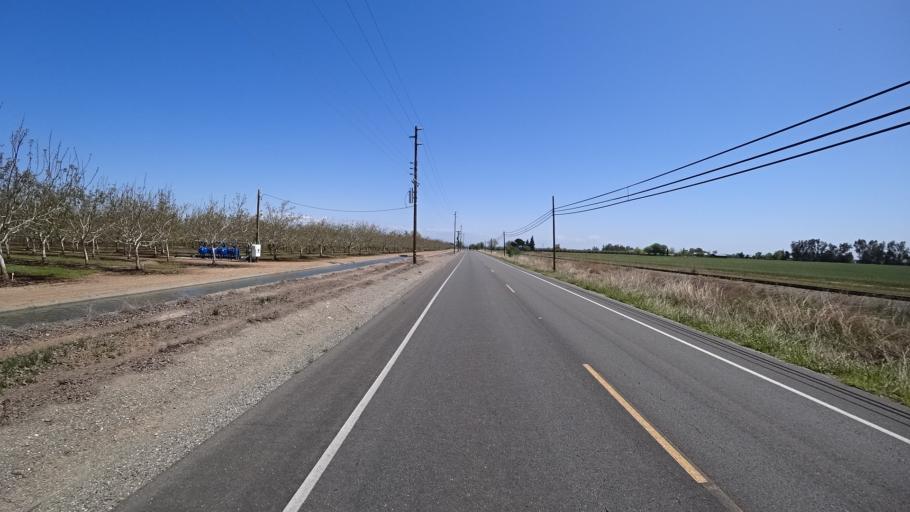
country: US
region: California
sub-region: Glenn County
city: Orland
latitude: 39.7689
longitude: -122.1740
